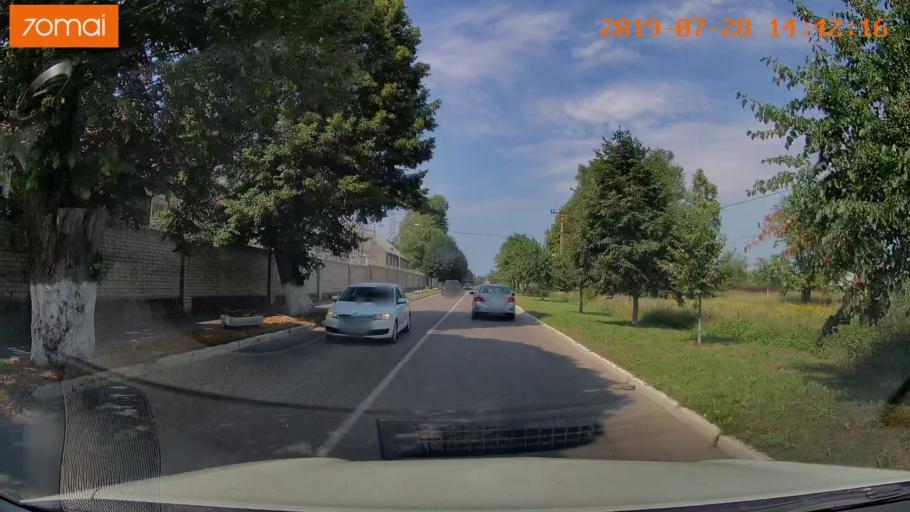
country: RU
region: Kaliningrad
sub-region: Gorod Kaliningrad
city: Yantarnyy
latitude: 54.8589
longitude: 19.9428
